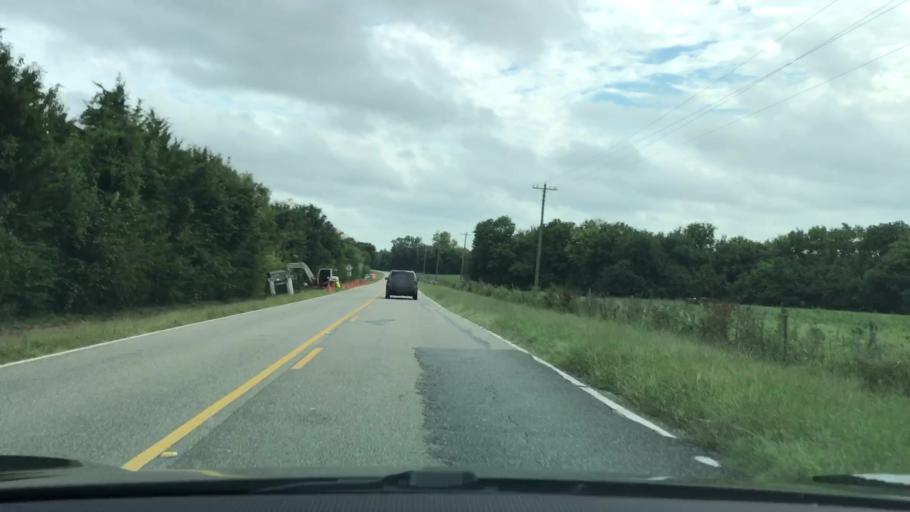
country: US
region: Alabama
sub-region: Montgomery County
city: Pike Road
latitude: 32.2903
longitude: -86.0760
